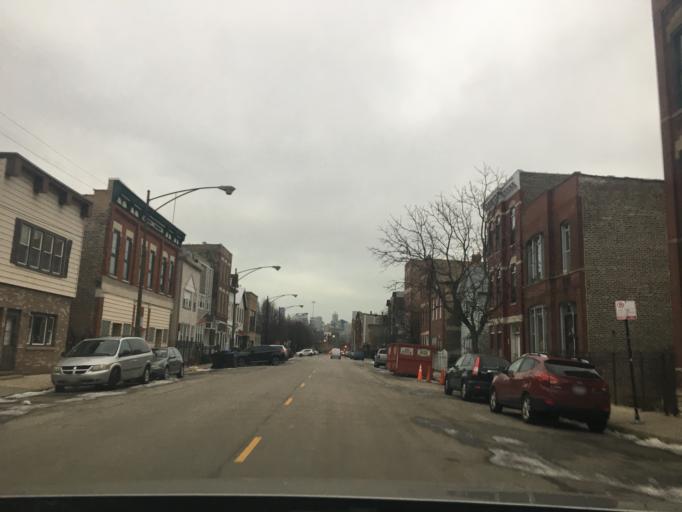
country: US
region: Illinois
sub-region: Cook County
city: Chicago
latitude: 41.8935
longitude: -87.6608
